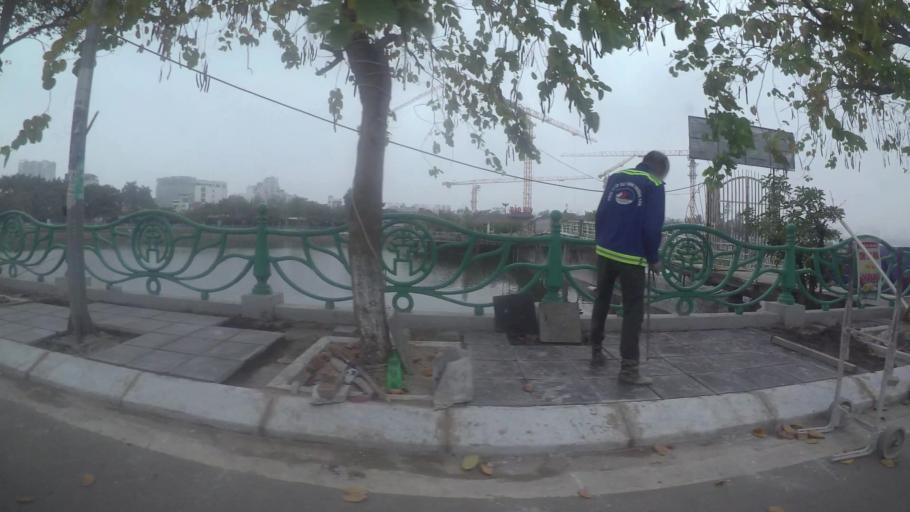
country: VN
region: Ha Noi
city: Tay Ho
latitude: 21.0663
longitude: 105.8216
